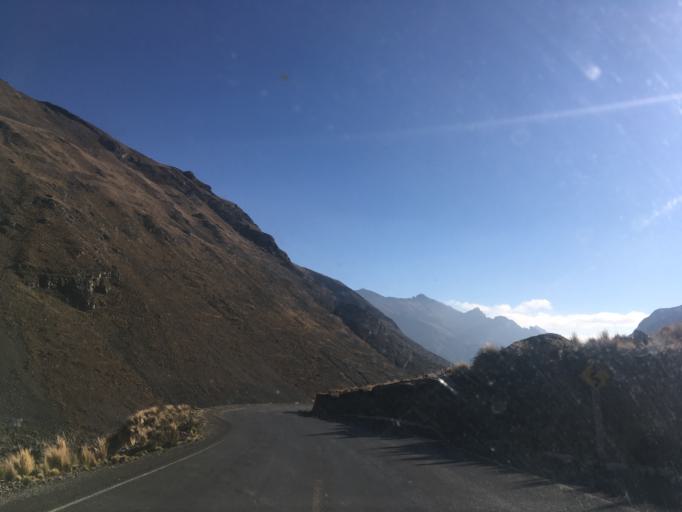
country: BO
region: La Paz
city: Quime
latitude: -17.0247
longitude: -67.2826
